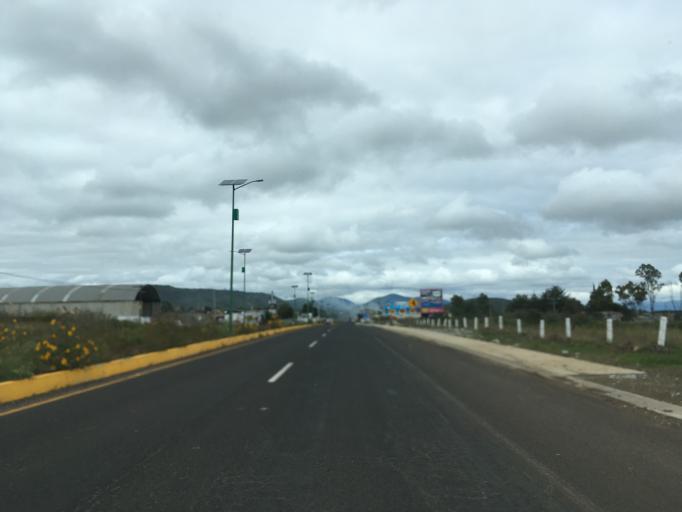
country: MX
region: Hidalgo
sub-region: Atotonilco el Grande
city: La Estancia
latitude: 20.3018
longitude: -98.6811
